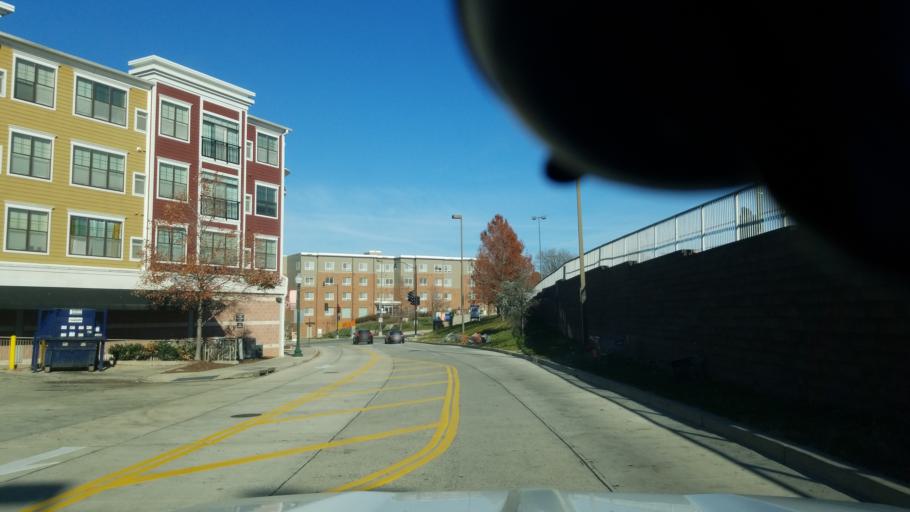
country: US
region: Maryland
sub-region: Prince George's County
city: Mount Rainier
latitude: 38.9204
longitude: -76.9943
